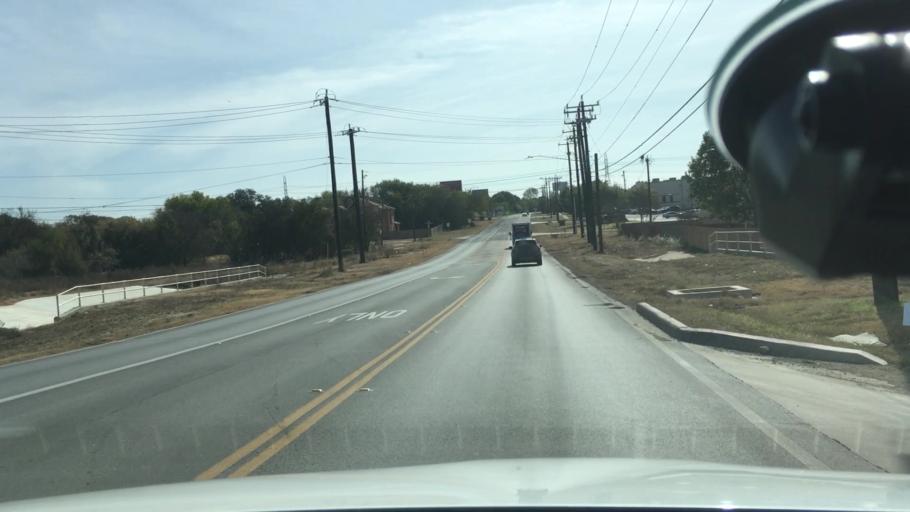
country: US
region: Texas
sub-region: Bexar County
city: Hollywood Park
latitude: 29.5789
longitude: -98.4202
